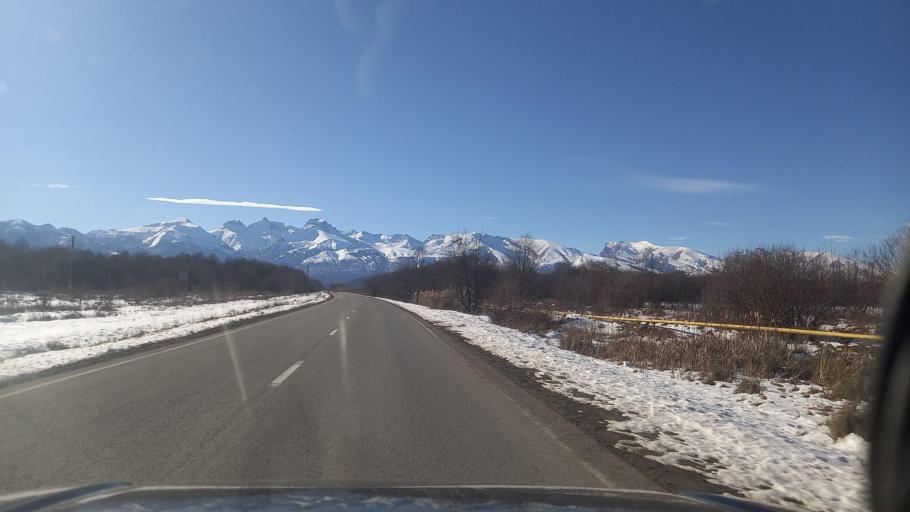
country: RU
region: North Ossetia
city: Chikola
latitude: 43.1638
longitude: 43.8555
